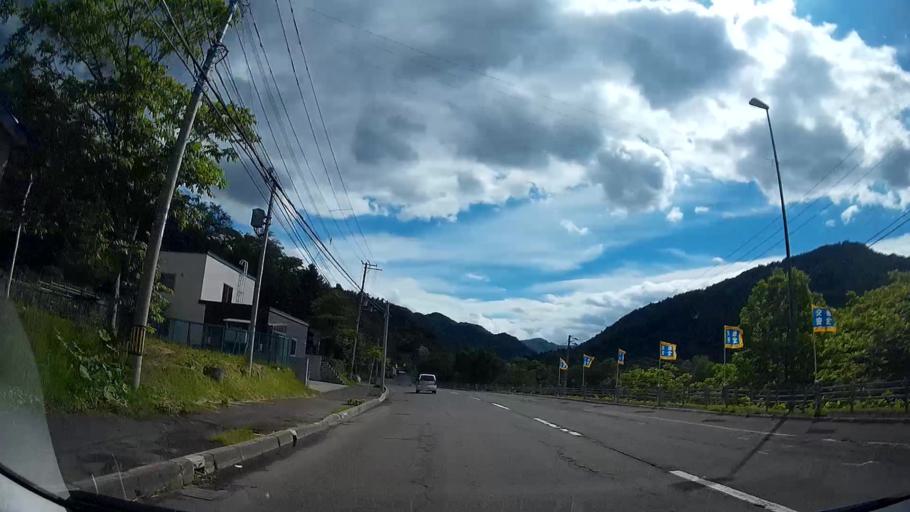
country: JP
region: Hokkaido
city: Sapporo
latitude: 42.9601
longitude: 141.1572
